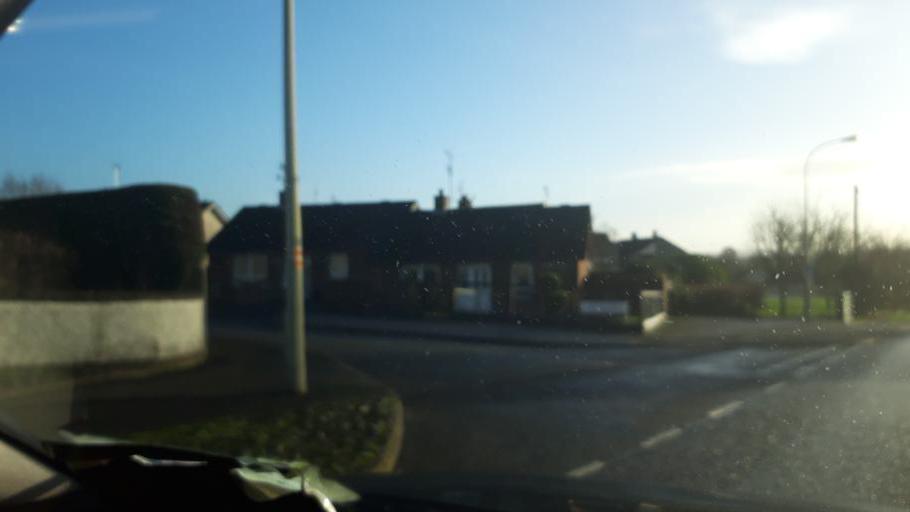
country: GB
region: Northern Ireland
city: Maghera
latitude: 54.8428
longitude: -6.6757
